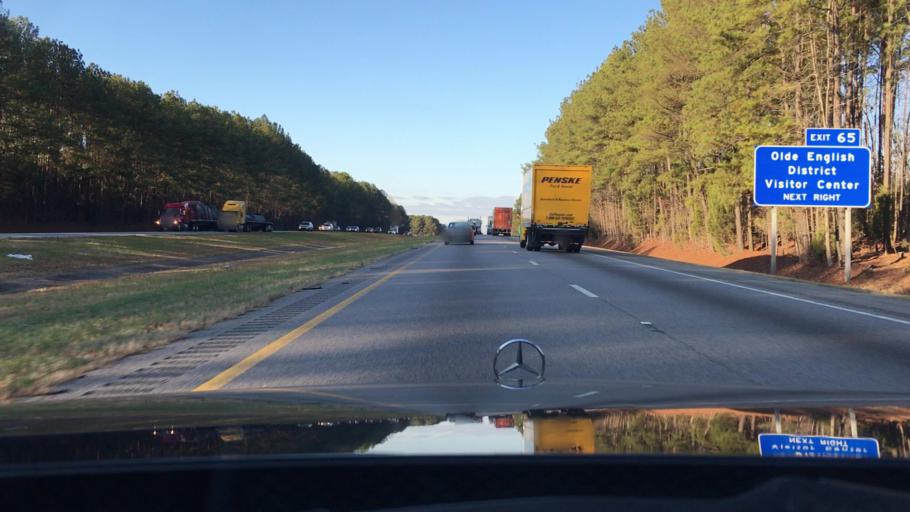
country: US
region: South Carolina
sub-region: Chester County
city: Eureka Mill
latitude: 34.7371
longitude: -81.0346
